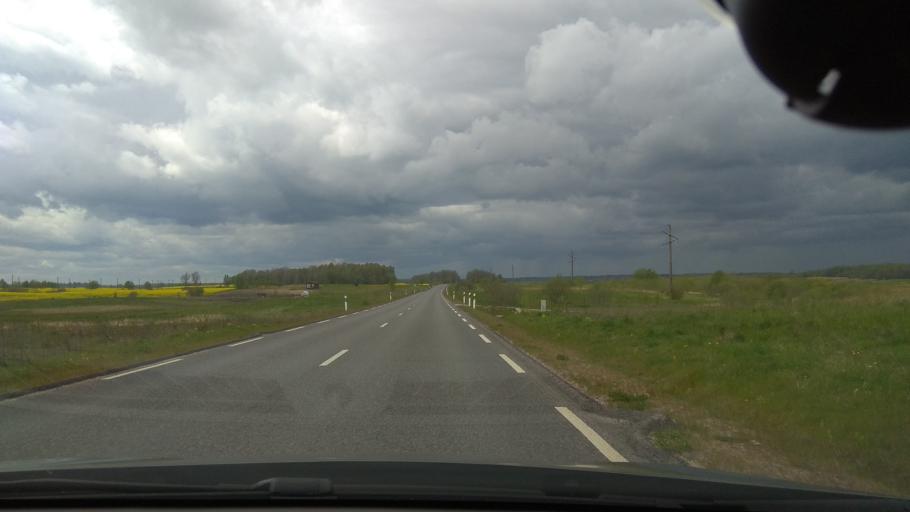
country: LT
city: Grigiskes
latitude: 54.8677
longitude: 25.0446
